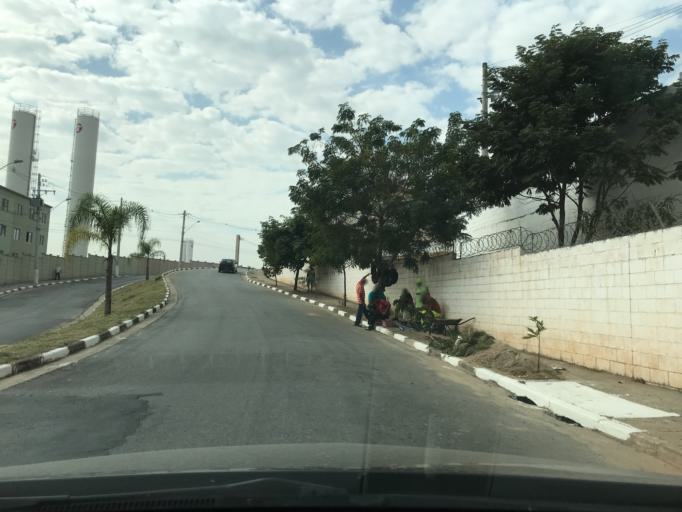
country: BR
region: Sao Paulo
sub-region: Cotia
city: Cotia
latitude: -23.6165
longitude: -46.9298
